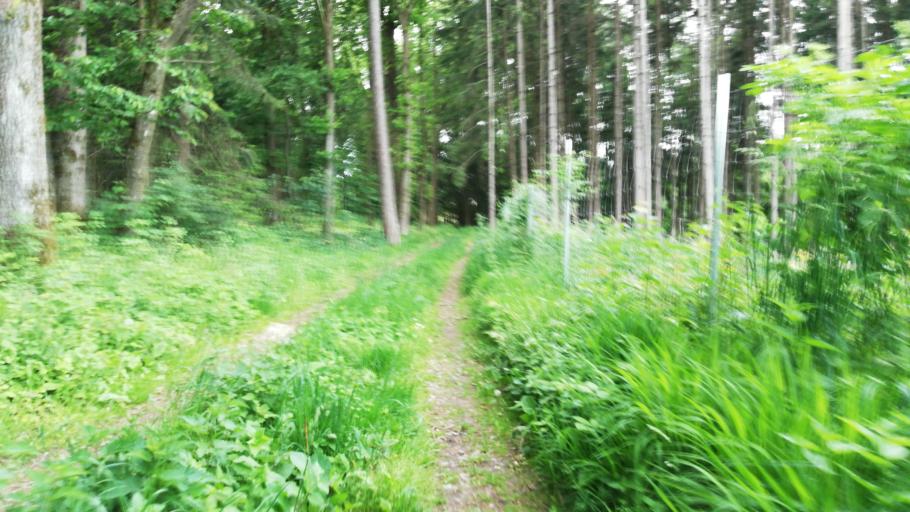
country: AT
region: Upper Austria
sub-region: Wels-Land
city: Gunskirchen
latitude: 48.1796
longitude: 13.9435
